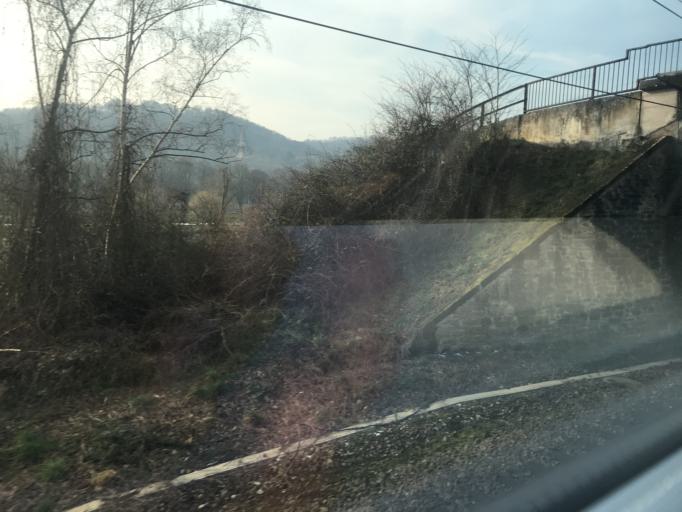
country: DE
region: Rheinland-Pfalz
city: Winningen
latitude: 50.3094
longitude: 7.5050
